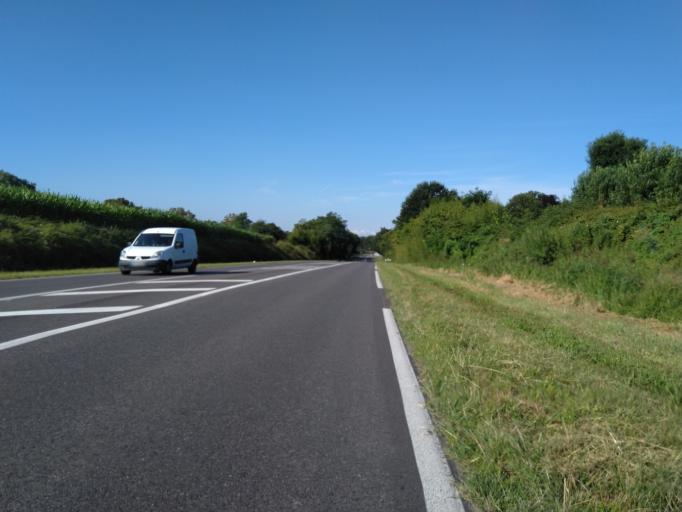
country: FR
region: Aquitaine
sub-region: Departement des Landes
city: Saint-Vincent-de-Paul
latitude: 43.7355
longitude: -1.0283
